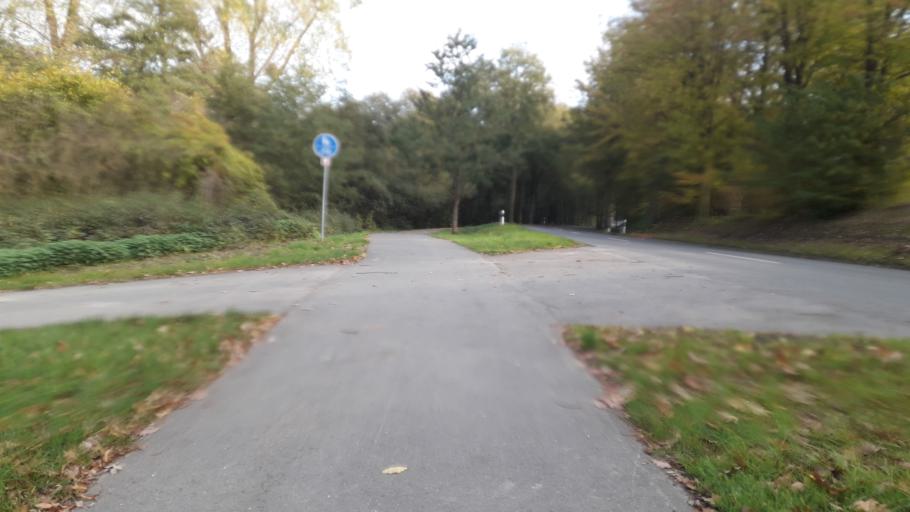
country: DE
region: North Rhine-Westphalia
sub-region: Regierungsbezirk Detmold
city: Paderborn
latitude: 51.6749
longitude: 8.7081
